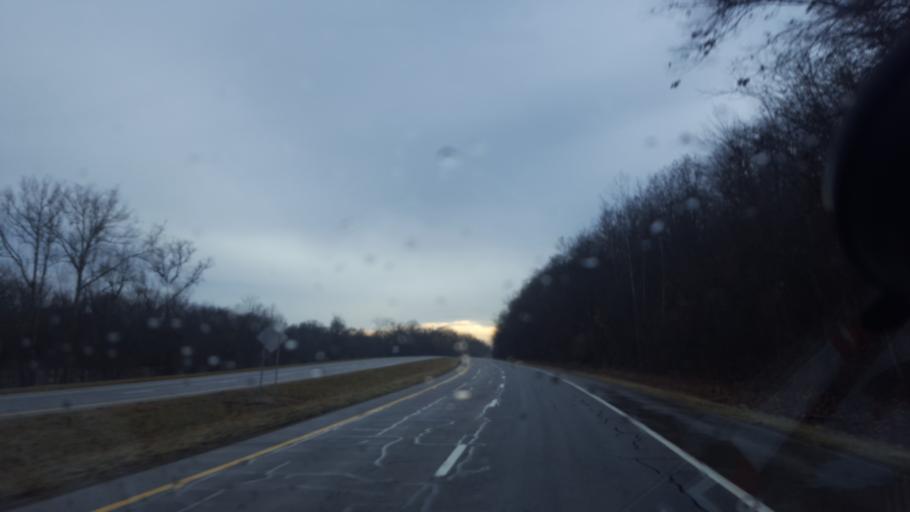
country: US
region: Ohio
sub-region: Coshocton County
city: West Lafayette
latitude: 40.2874
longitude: -81.6904
